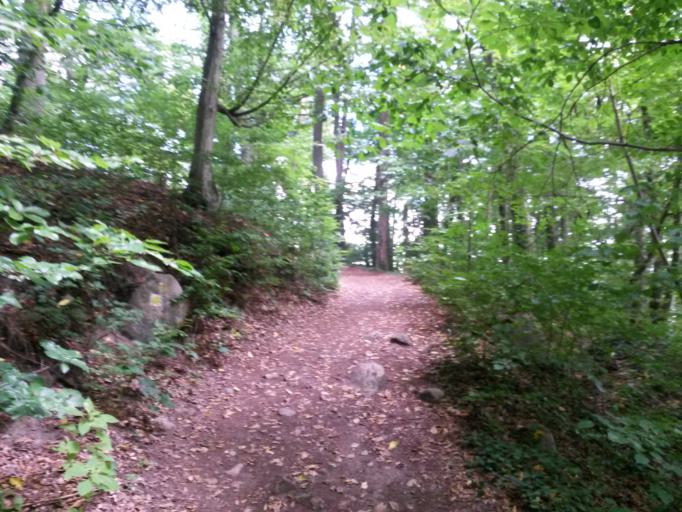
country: DE
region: Brandenburg
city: Chorin
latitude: 52.8947
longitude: 13.8831
